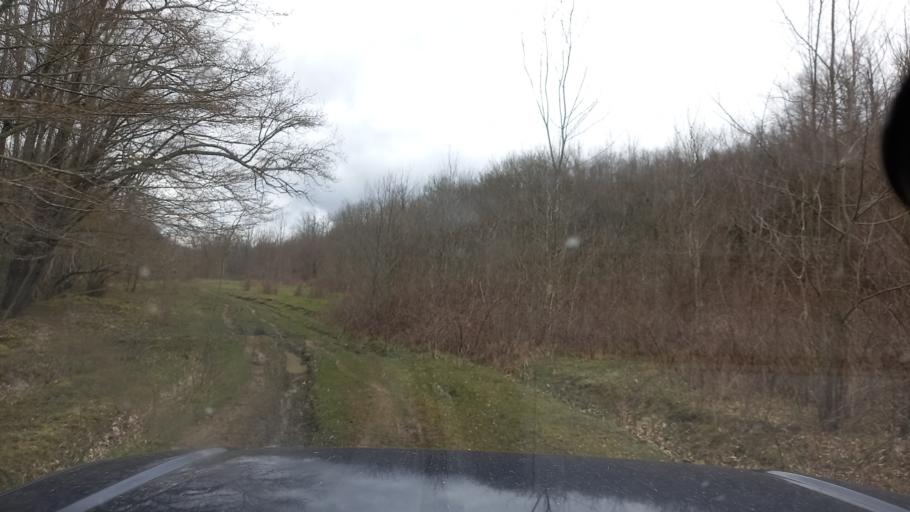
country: RU
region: Krasnodarskiy
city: Pshada
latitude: 44.4857
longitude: 38.3995
